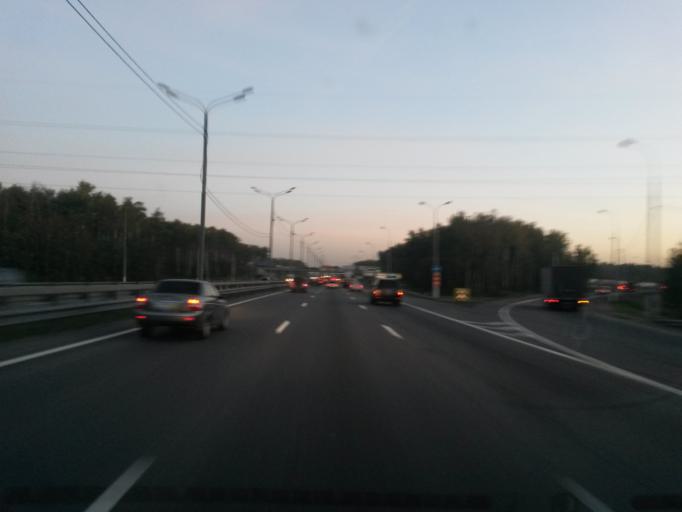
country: RU
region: Moskovskaya
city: Belyye Stolby
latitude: 55.3429
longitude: 37.8077
